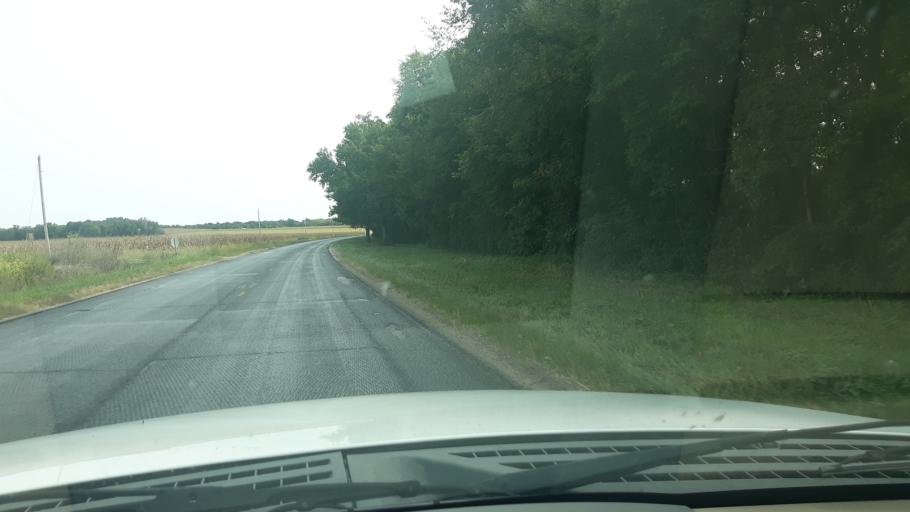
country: US
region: Illinois
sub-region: Edwards County
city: Grayville
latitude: 38.2911
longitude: -87.9744
